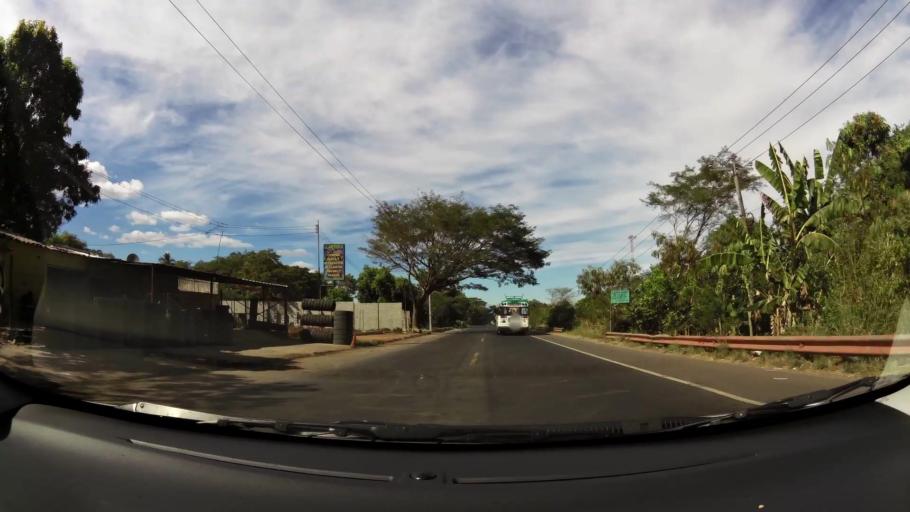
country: SV
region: San Salvador
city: Guazapa
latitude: 13.9134
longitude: -89.1823
